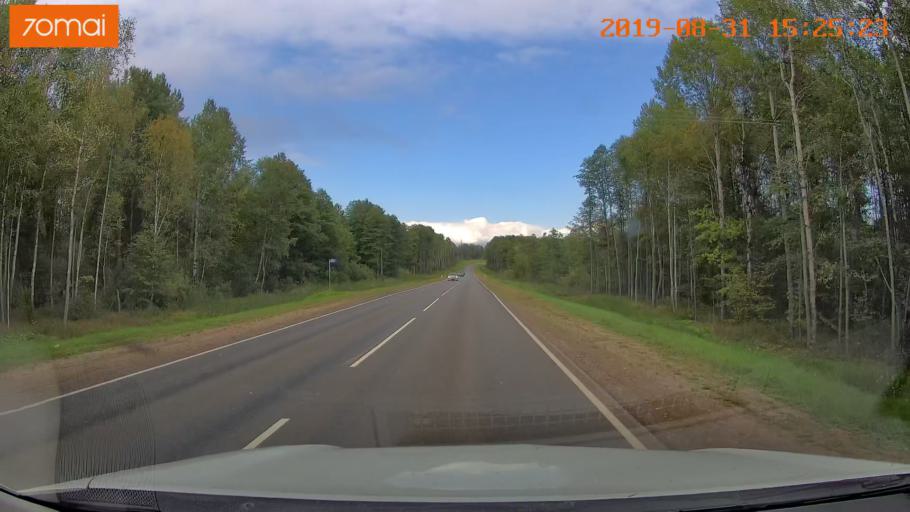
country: RU
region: Kaluga
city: Baryatino
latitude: 54.5408
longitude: 34.5190
